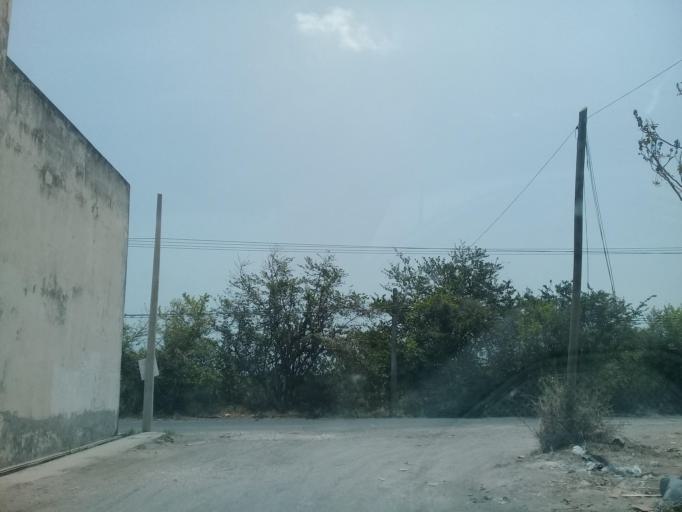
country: MX
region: Veracruz
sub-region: Veracruz
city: Hacienda Sotavento
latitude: 19.1342
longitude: -96.1780
